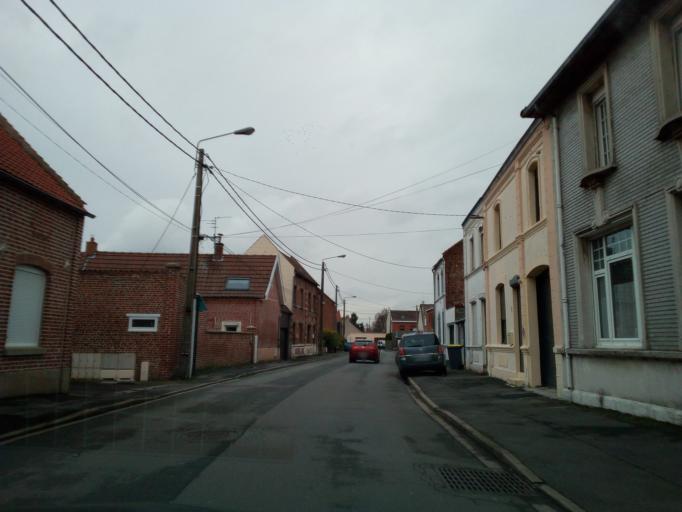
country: FR
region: Nord-Pas-de-Calais
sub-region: Departement du Pas-de-Calais
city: Billy-Berclau
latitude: 50.5232
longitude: 2.8732
